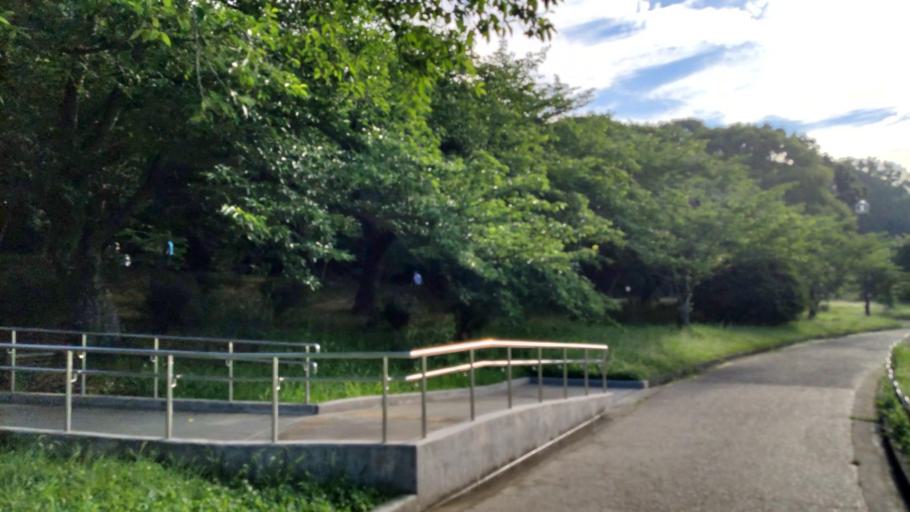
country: JP
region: Hyogo
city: Akashi
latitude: 34.6573
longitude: 134.9932
